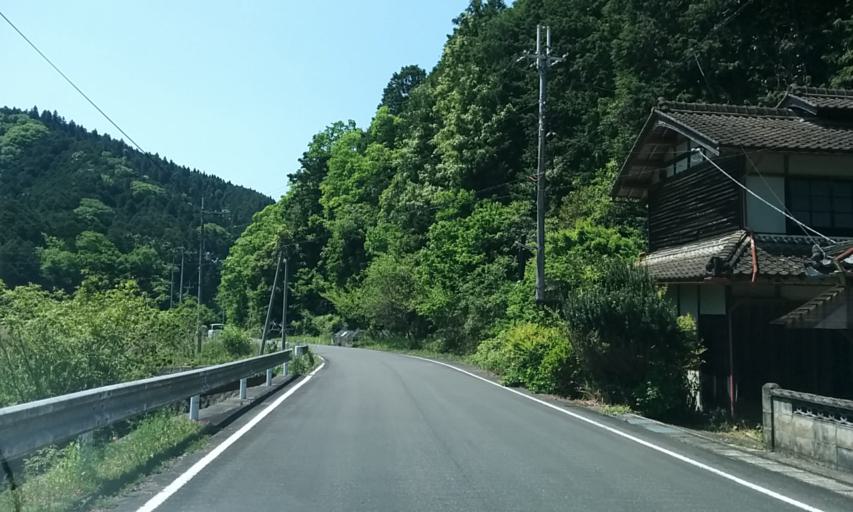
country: JP
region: Kyoto
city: Ayabe
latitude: 35.3821
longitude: 135.1891
